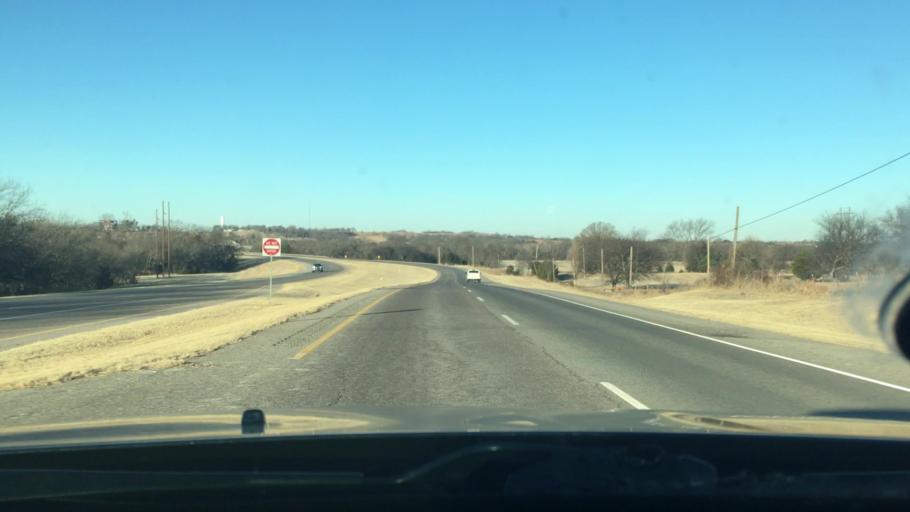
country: US
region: Oklahoma
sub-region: Murray County
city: Sulphur
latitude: 34.5068
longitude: -97.0261
